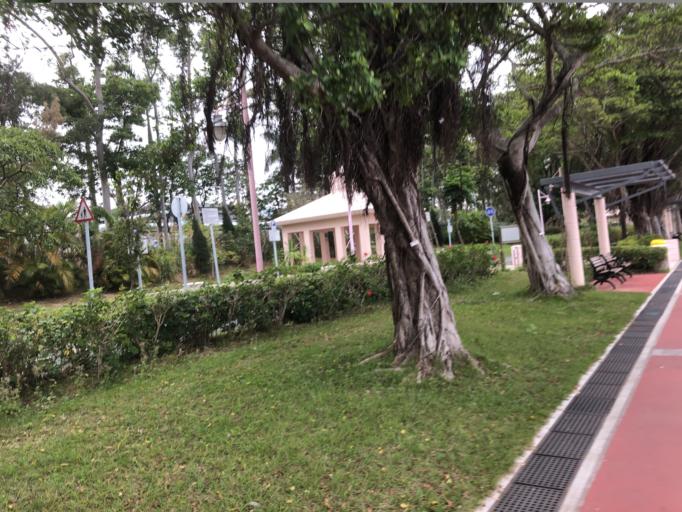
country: HK
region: Tai Po
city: Tai Po
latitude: 22.4527
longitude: 114.1839
